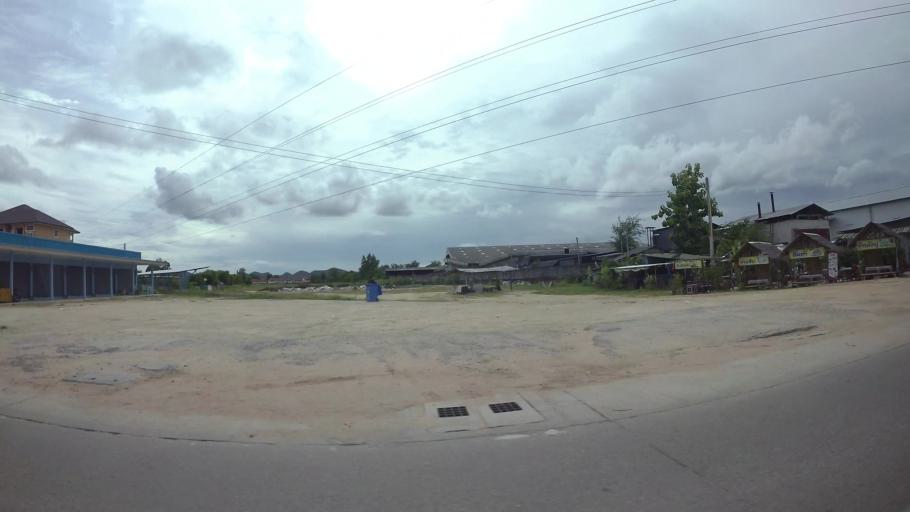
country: TH
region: Chon Buri
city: Si Racha
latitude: 13.1462
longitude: 100.9771
